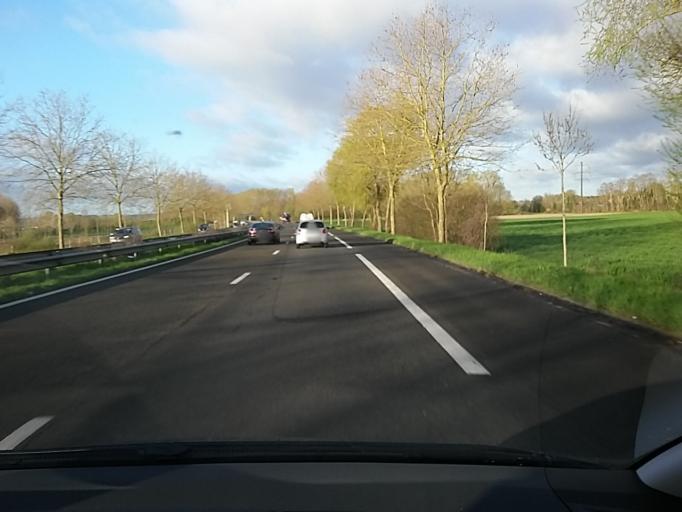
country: FR
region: Picardie
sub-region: Departement de l'Oise
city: Le Meux
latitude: 49.3486
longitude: 2.7440
